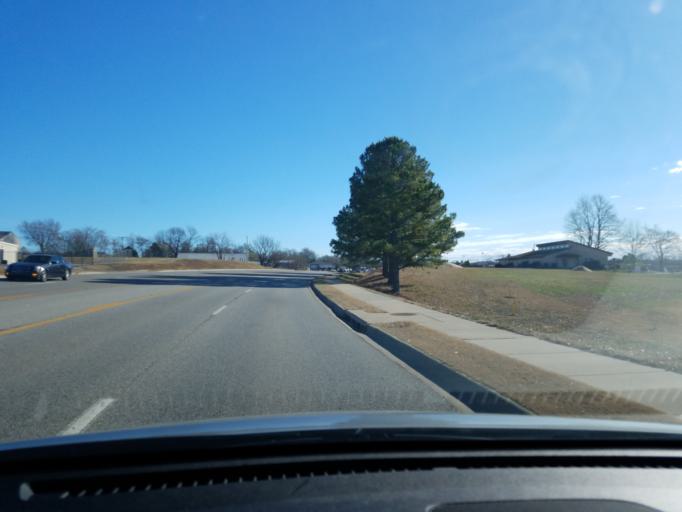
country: US
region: Arkansas
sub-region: Carroll County
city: Berryville
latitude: 36.3821
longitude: -93.5969
